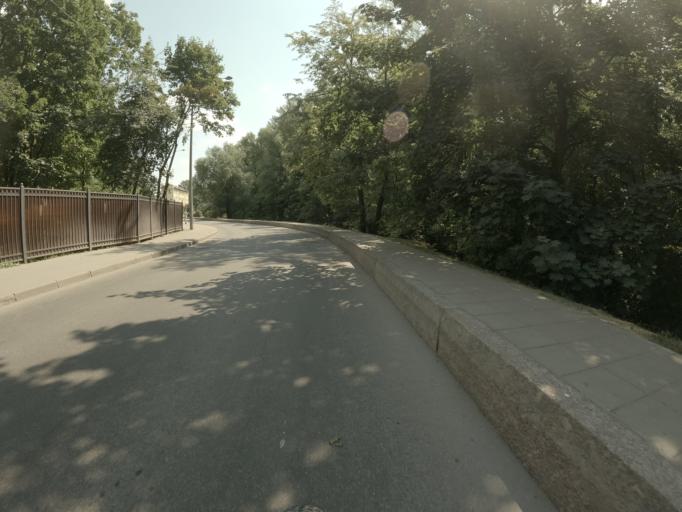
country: RU
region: St.-Petersburg
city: Admiralteisky
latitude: 59.9046
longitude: 30.2669
